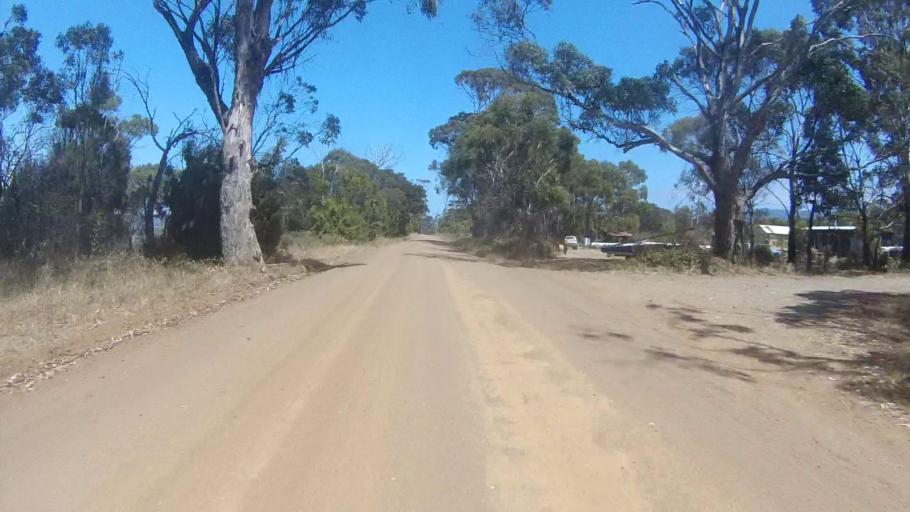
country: AU
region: Tasmania
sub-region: Sorell
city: Sorell
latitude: -42.8335
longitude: 147.8554
